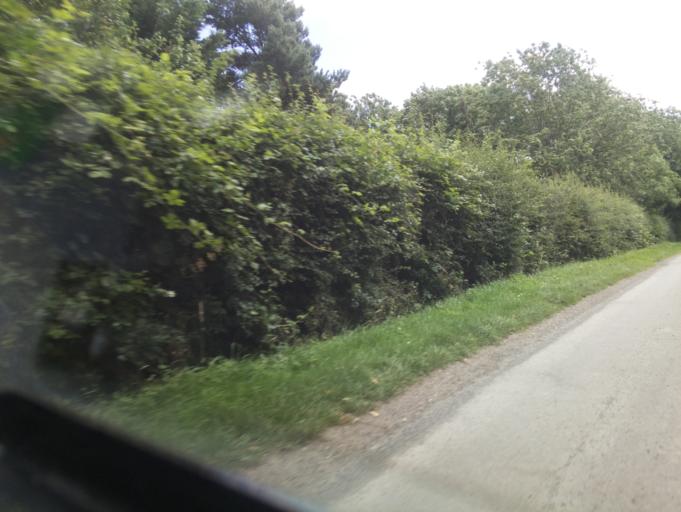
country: GB
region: England
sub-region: Nottinghamshire
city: Cotgrave
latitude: 52.8627
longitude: -1.0600
